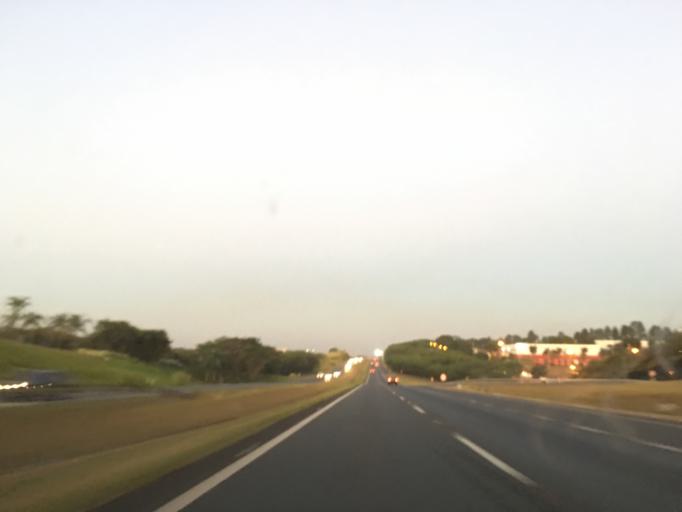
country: BR
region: Sao Paulo
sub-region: Piracicaba
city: Piracicaba
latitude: -22.7229
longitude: -47.5949
